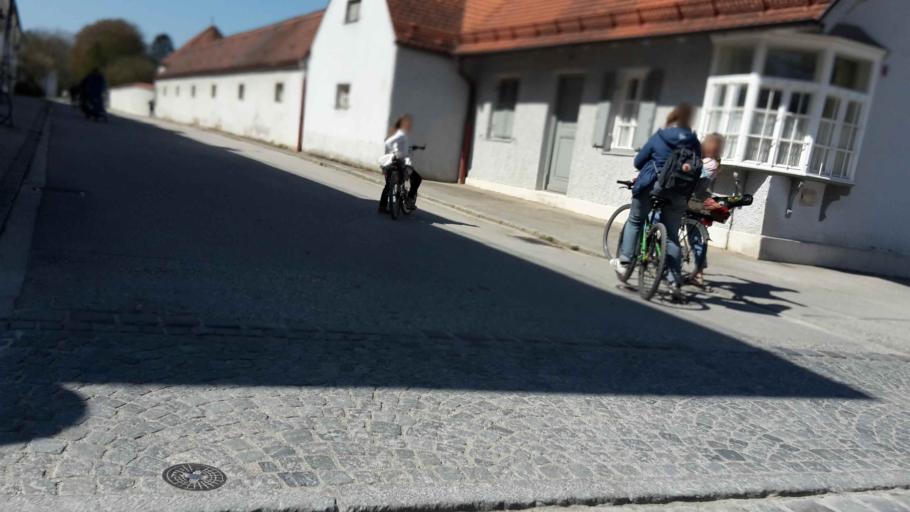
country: DE
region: Bavaria
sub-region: Upper Bavaria
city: Pasing
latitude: 48.1611
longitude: 11.5053
